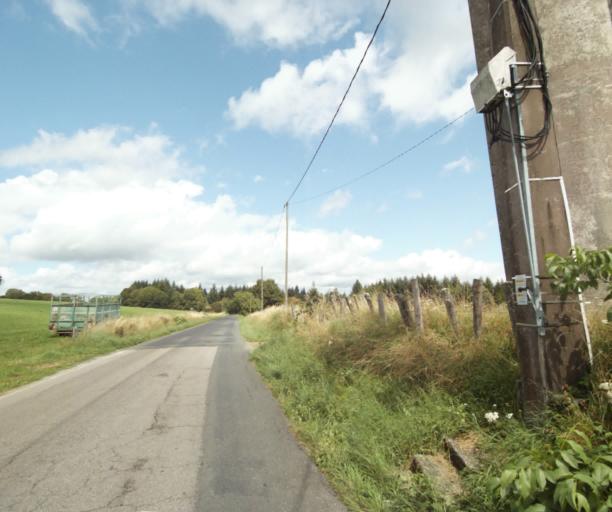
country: FR
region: Limousin
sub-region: Departement de la Correze
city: Sainte-Fortunade
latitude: 45.1900
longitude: 1.8140
